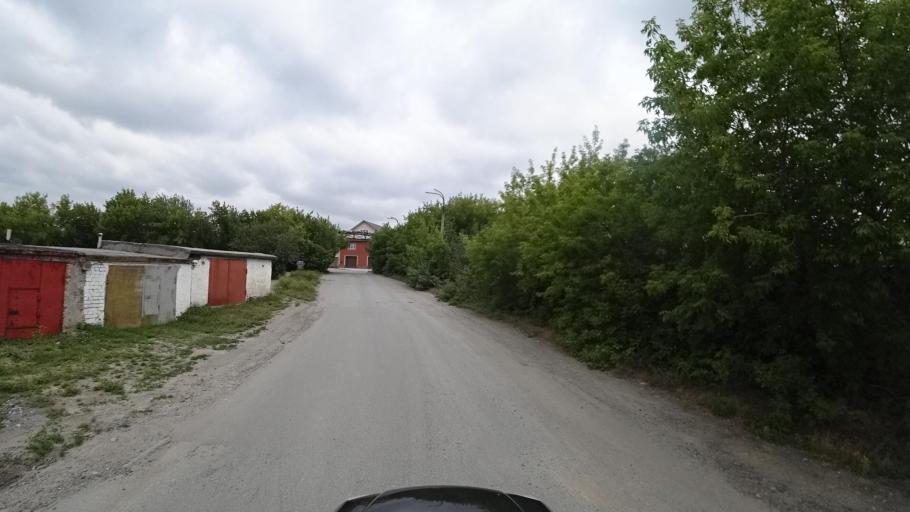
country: RU
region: Sverdlovsk
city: Kamyshlov
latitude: 56.8346
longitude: 62.7193
